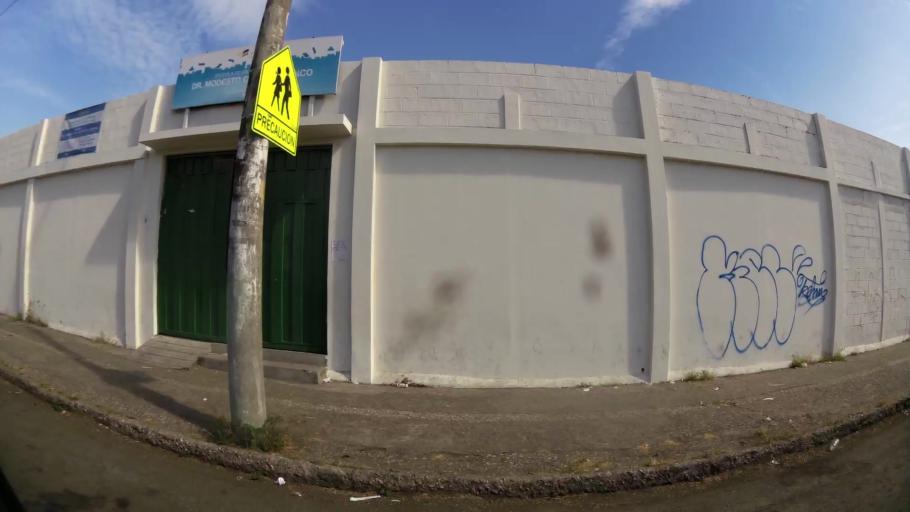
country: EC
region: Guayas
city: Guayaquil
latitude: -2.2193
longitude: -79.8973
